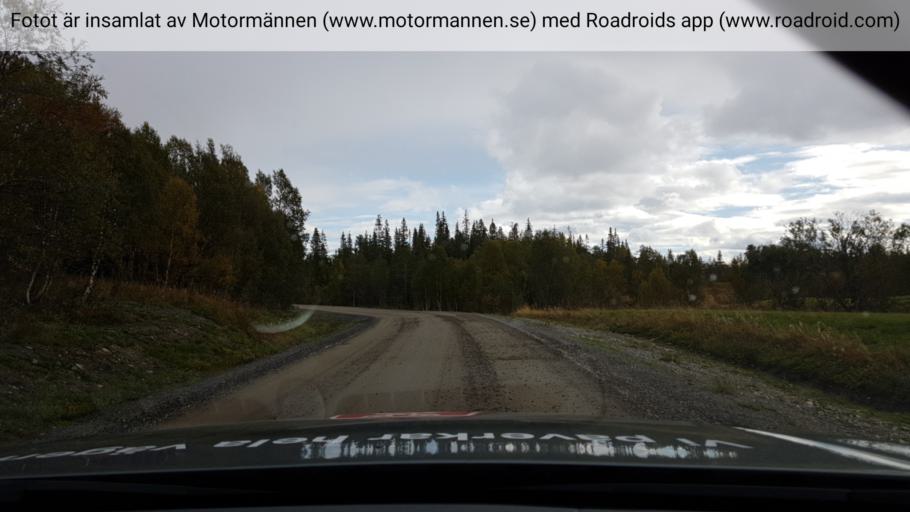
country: NO
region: Nord-Trondelag
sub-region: Snasa
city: Snaase
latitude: 63.7076
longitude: 12.3554
